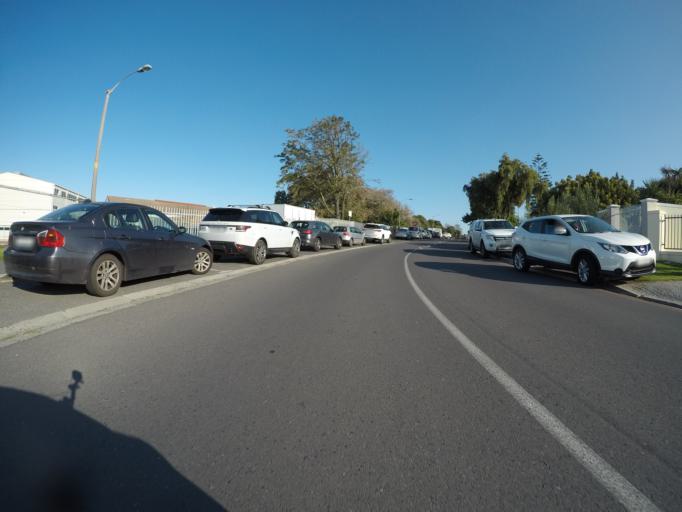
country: ZA
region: Western Cape
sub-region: City of Cape Town
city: Kraaifontein
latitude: -33.8533
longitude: 18.6576
